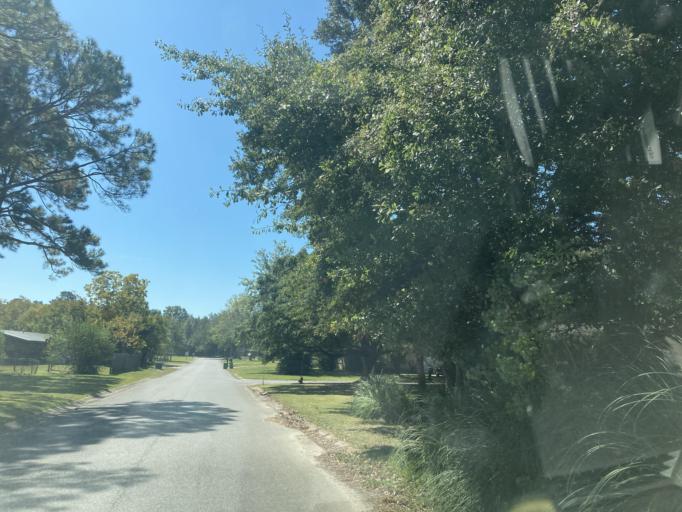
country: US
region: Mississippi
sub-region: Jackson County
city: Saint Martin
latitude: 30.4521
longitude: -88.8645
